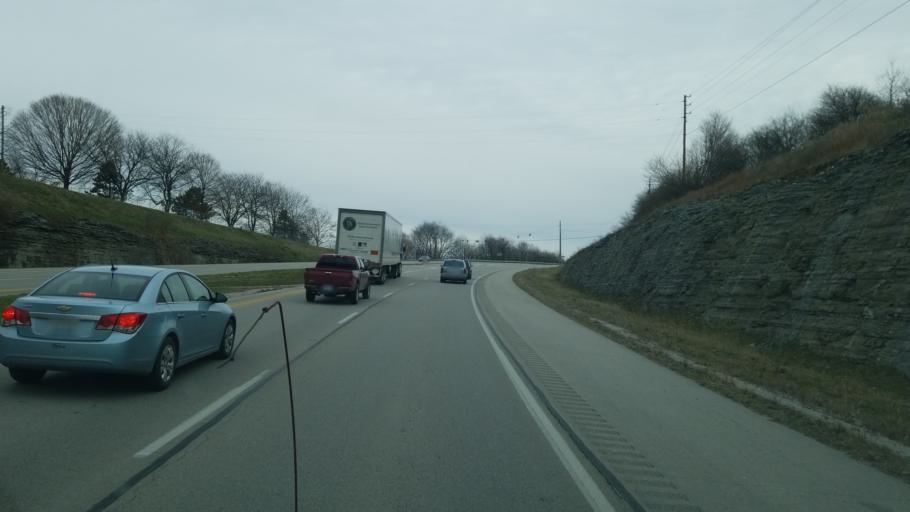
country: US
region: Kentucky
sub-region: Bourbon County
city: Paris
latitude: 38.2269
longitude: -84.2492
